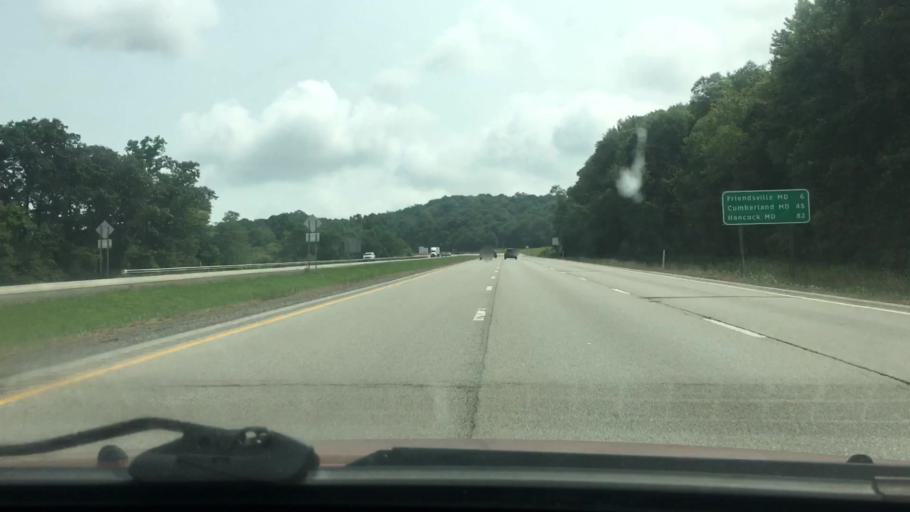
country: US
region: West Virginia
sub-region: Preston County
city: Terra Alta
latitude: 39.6575
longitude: -79.5170
